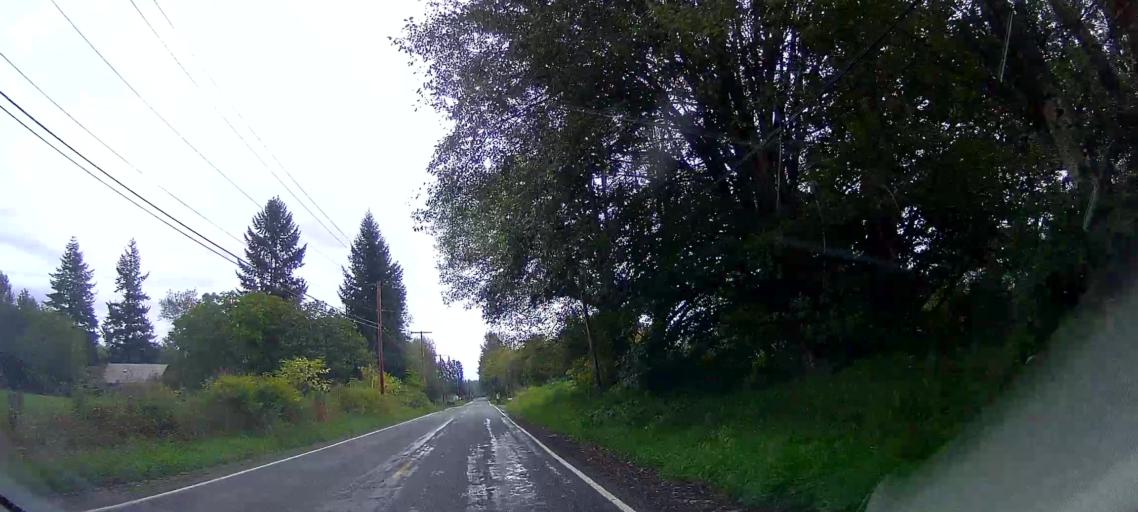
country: US
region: Washington
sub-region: Skagit County
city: Sedro-Woolley
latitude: 48.5273
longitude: -122.0441
